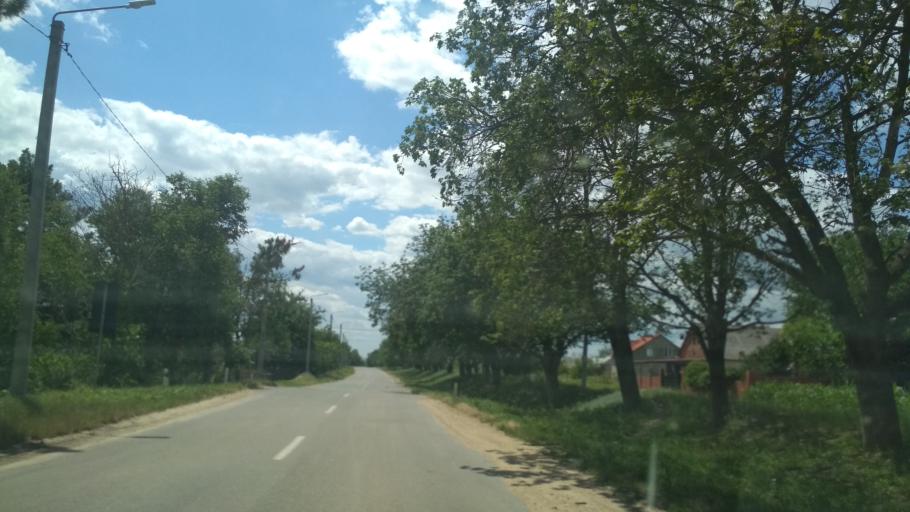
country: MD
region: Criuleni
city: Criuleni
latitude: 47.1746
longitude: 29.1969
